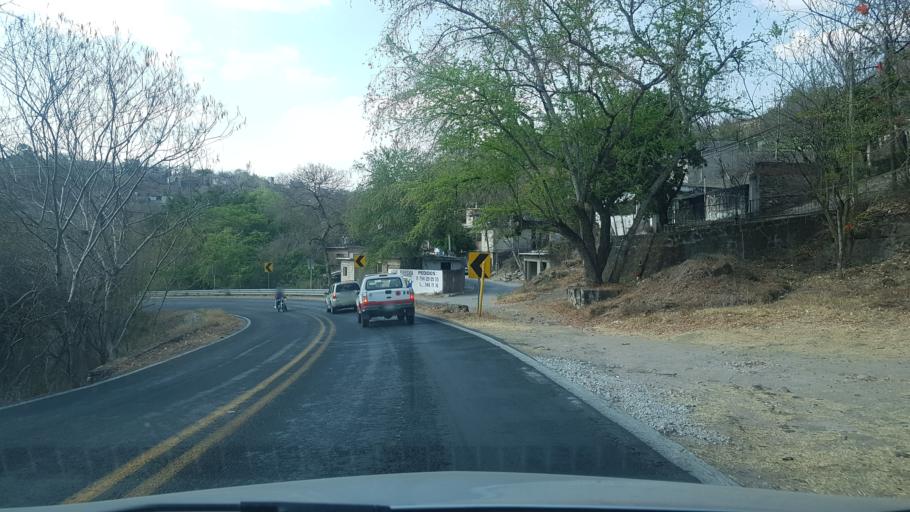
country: MX
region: Morelos
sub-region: Amacuzac
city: Amacuzac
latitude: 18.6041
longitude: -99.3673
